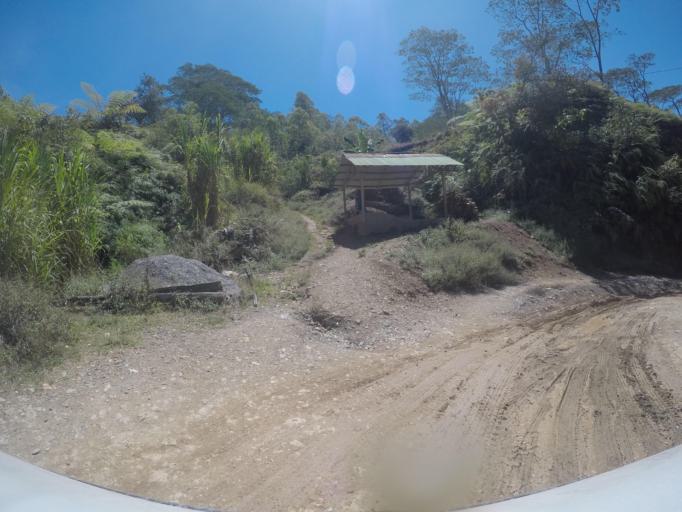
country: TL
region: Ermera
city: Gleno
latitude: -8.7728
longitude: 125.3985
